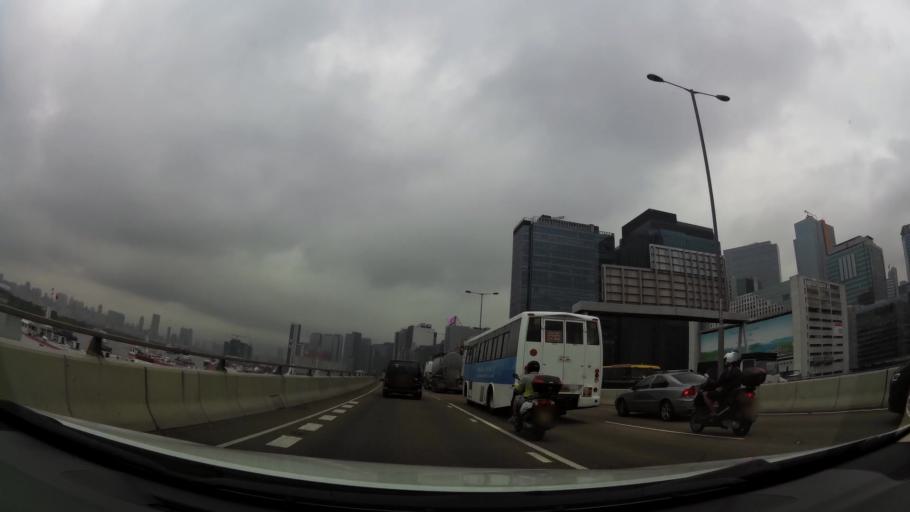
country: HK
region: Kowloon City
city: Kowloon
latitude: 22.3073
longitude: 114.2212
